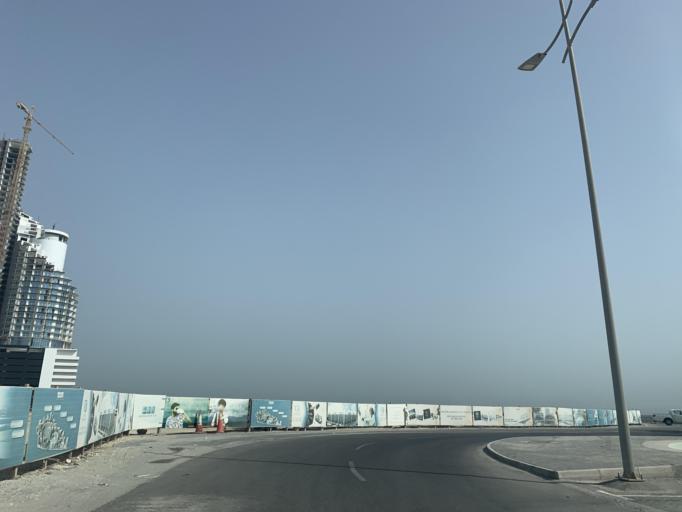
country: BH
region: Manama
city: Jidd Hafs
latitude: 26.2430
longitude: 50.5568
